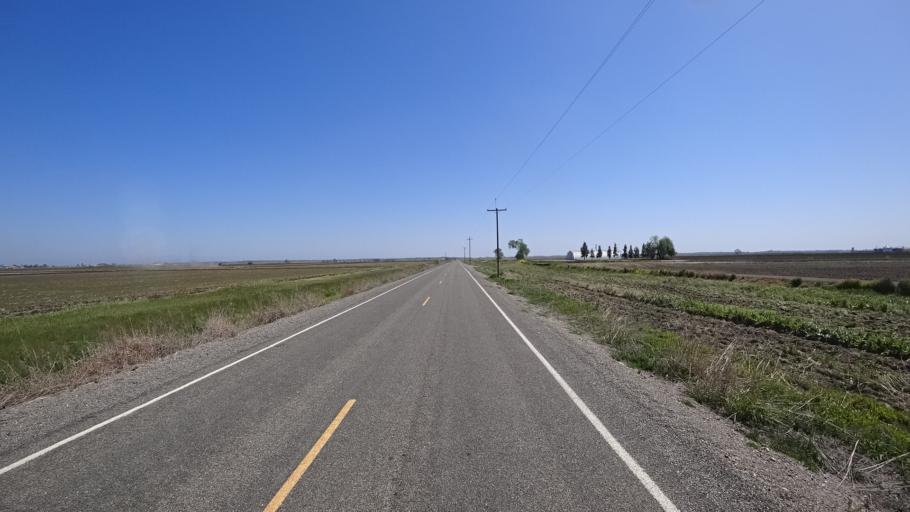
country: US
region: California
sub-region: Glenn County
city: Willows
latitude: 39.5581
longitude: -122.0528
